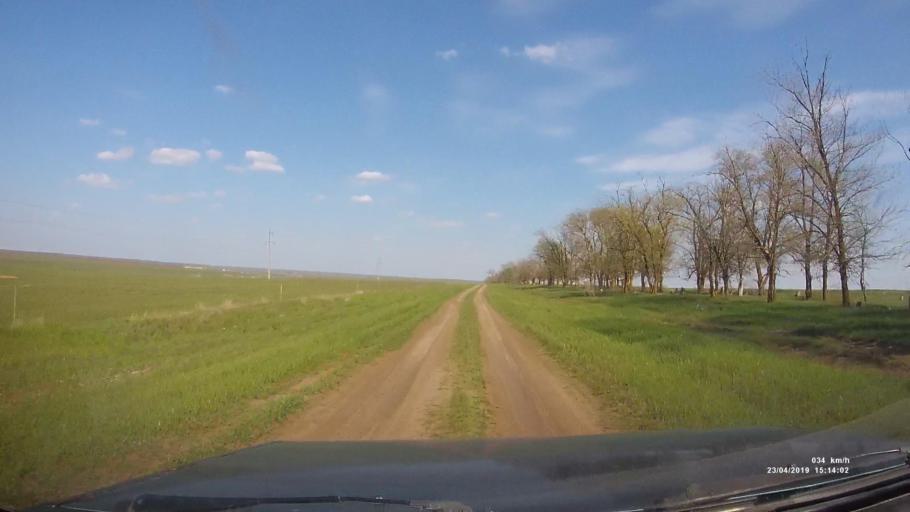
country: RU
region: Rostov
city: Remontnoye
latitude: 46.5397
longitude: 42.9601
